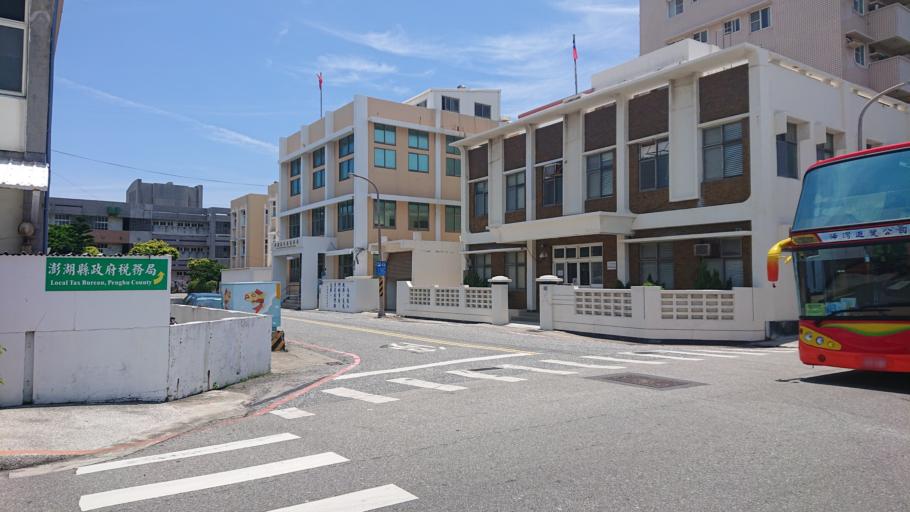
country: TW
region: Taiwan
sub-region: Penghu
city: Ma-kung
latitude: 23.5697
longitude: 119.5659
